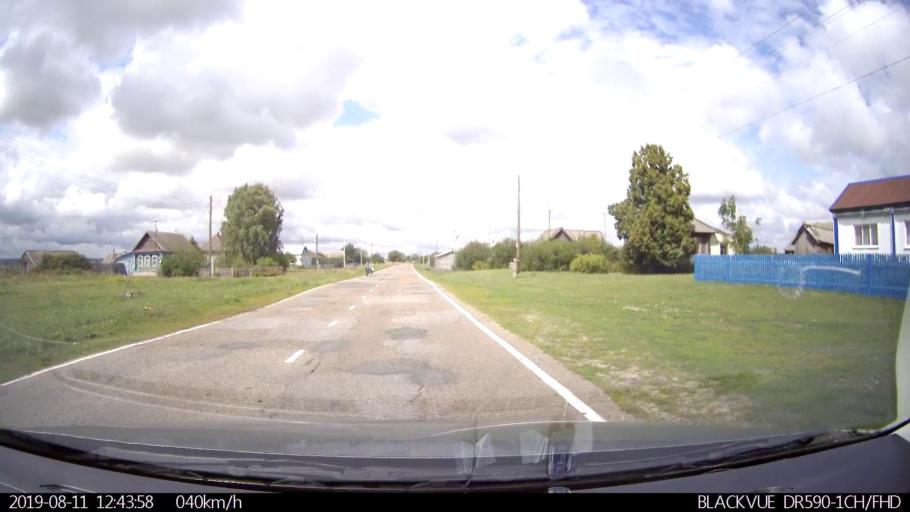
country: RU
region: Ulyanovsk
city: Ignatovka
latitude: 53.8528
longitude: 47.7396
